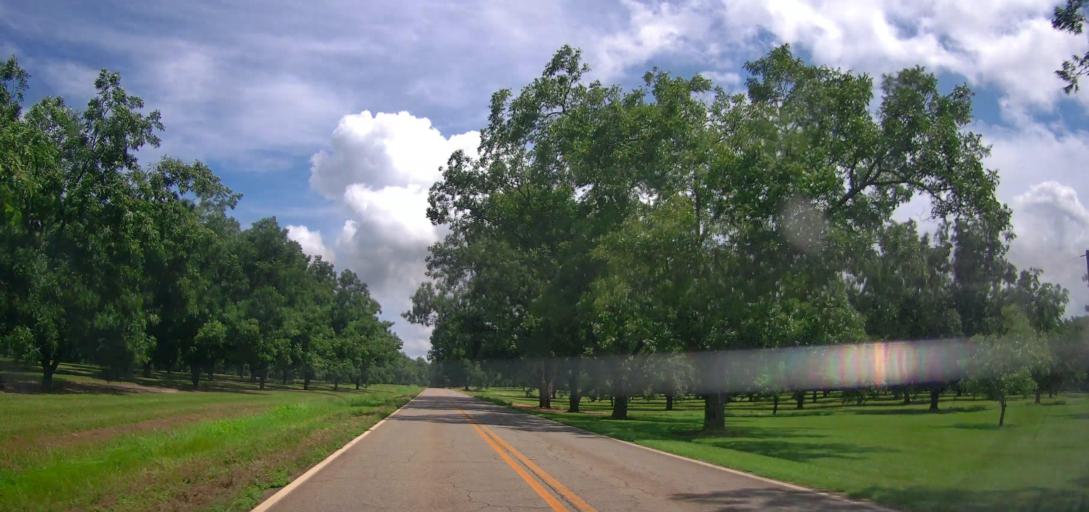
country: US
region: Georgia
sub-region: Houston County
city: Perry
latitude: 32.5212
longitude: -83.7960
